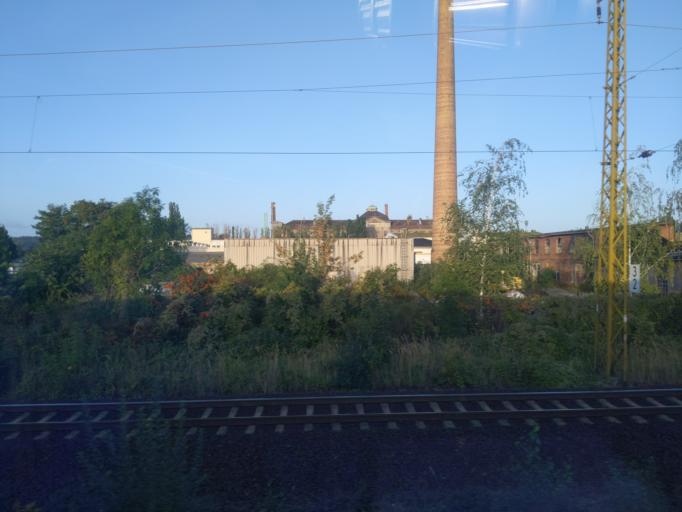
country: DE
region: Saxony
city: Coswig
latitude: 51.1321
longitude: 13.5715
